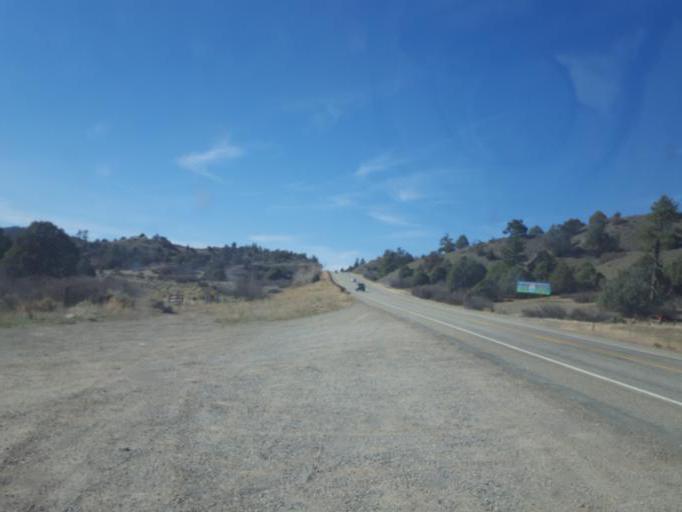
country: US
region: Colorado
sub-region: Archuleta County
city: Pagosa Springs
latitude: 37.2086
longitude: -107.2485
